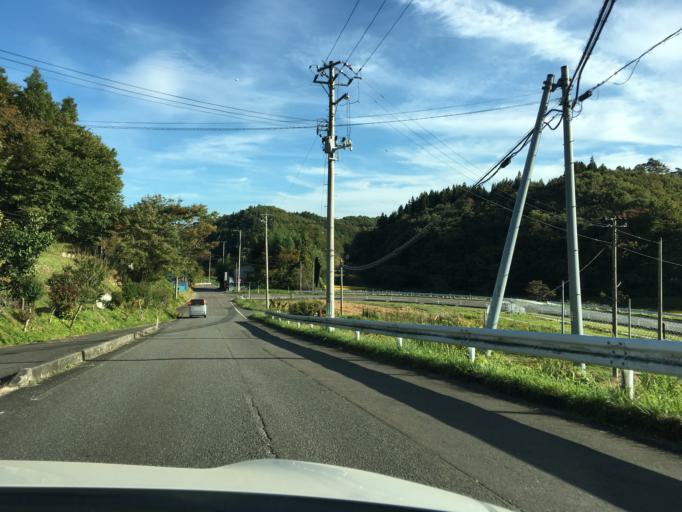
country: JP
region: Fukushima
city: Funehikimachi-funehiki
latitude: 37.2647
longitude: 140.6071
